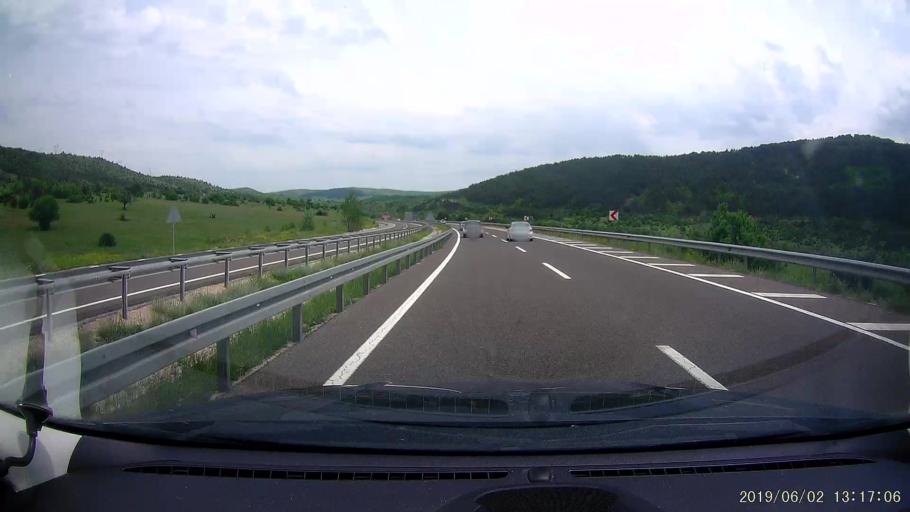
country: TR
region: Karabuk
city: Gozyeri
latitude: 40.8425
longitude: 32.6949
